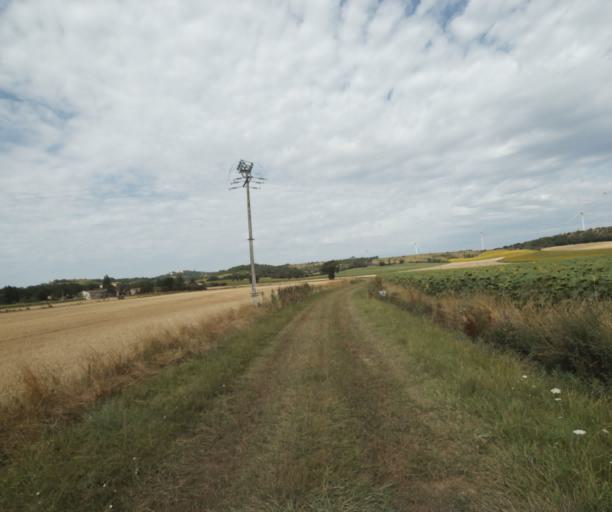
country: FR
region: Midi-Pyrenees
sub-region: Departement de la Haute-Garonne
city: Saint-Felix-Lauragais
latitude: 43.4519
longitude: 1.9211
